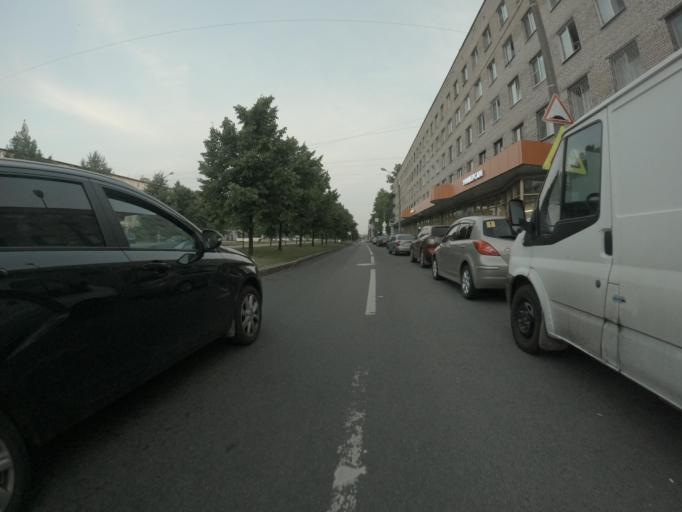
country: RU
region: Leningrad
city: Kalininskiy
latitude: 59.9759
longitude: 30.4013
